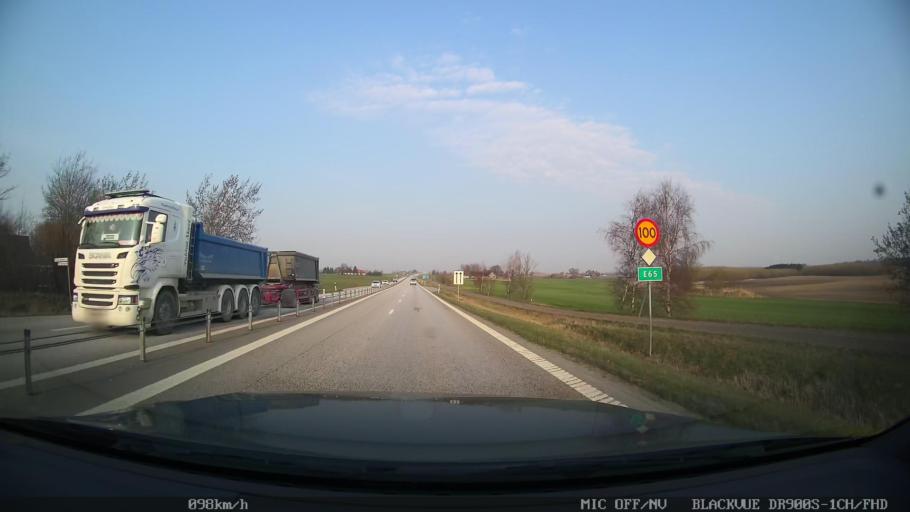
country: SE
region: Skane
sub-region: Skurups Kommun
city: Rydsgard
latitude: 55.4742
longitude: 13.6666
